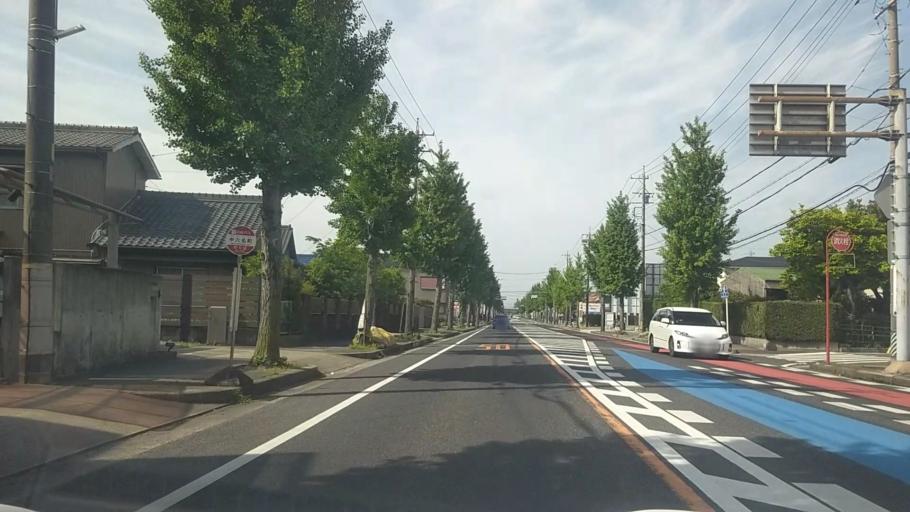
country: JP
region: Aichi
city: Okazaki
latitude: 34.9457
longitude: 137.1550
